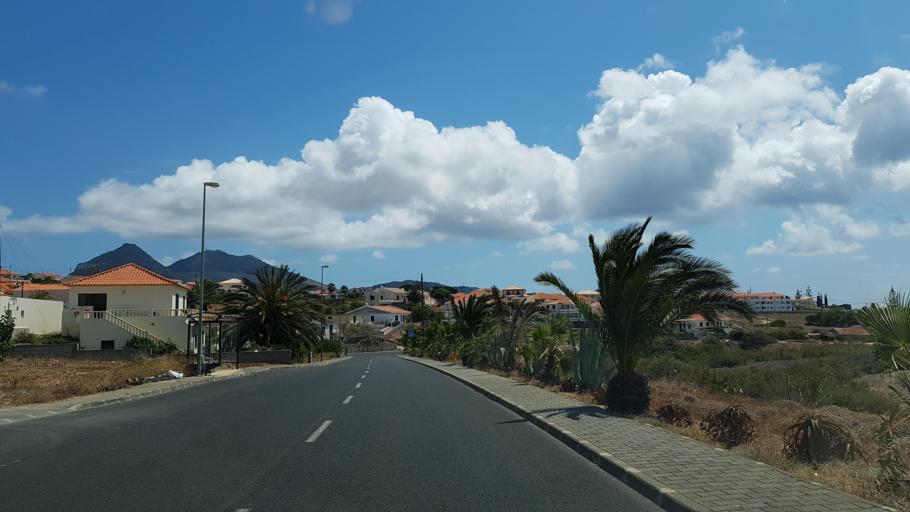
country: PT
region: Madeira
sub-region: Porto Santo
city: Vila de Porto Santo
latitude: 33.0529
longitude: -16.3593
